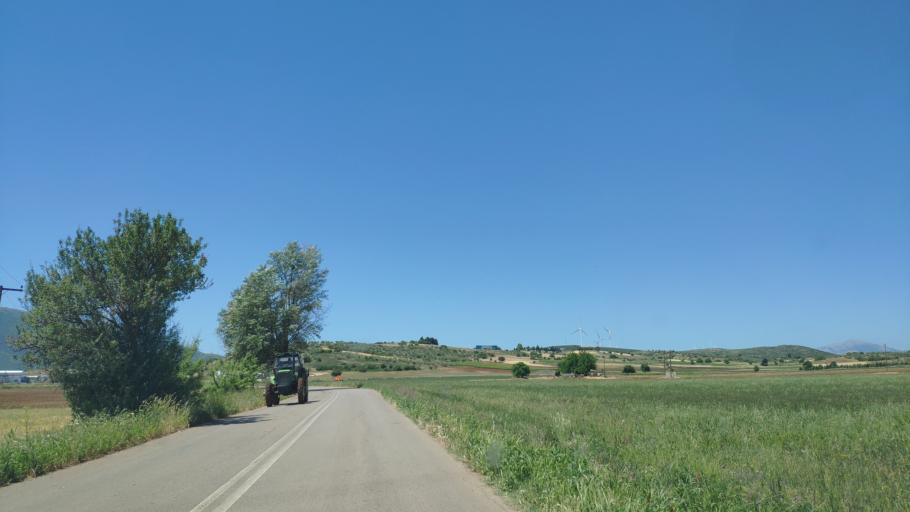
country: GR
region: Central Greece
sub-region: Nomos Voiotias
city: Kaparellion
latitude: 38.2446
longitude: 23.2361
